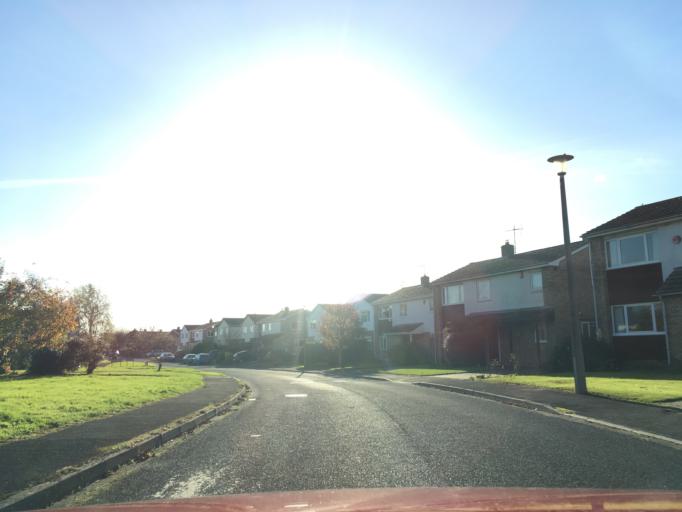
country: GB
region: England
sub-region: South Gloucestershire
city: Falfield
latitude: 51.6564
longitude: -2.4608
